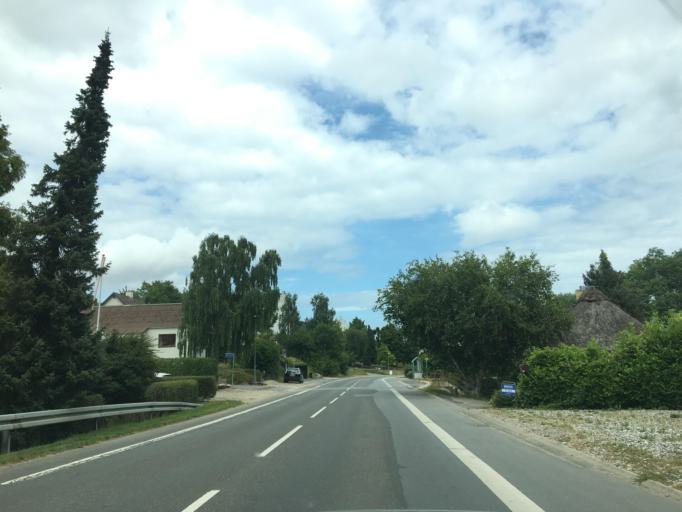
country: DK
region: South Denmark
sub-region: Nyborg Kommune
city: Nyborg
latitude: 55.3079
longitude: 10.7307
